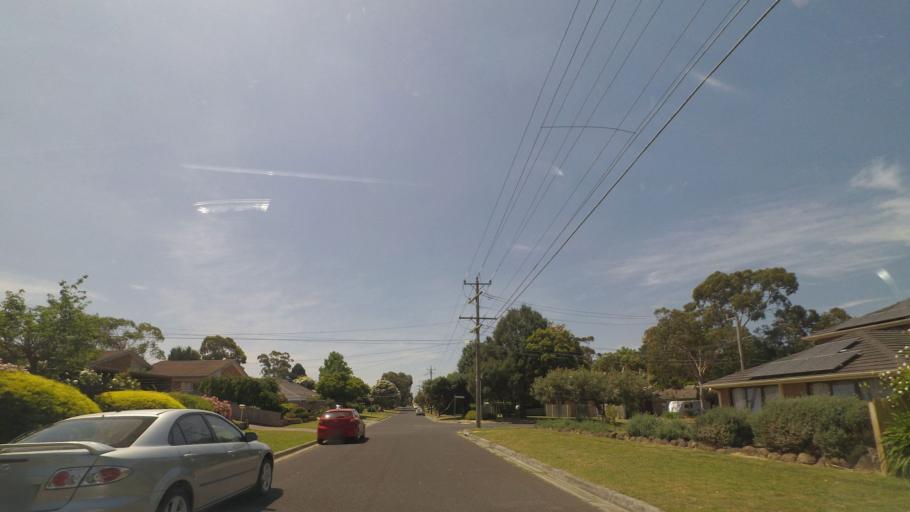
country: AU
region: Victoria
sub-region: Yarra Ranges
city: Chirnside Park
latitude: -37.7532
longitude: 145.3076
